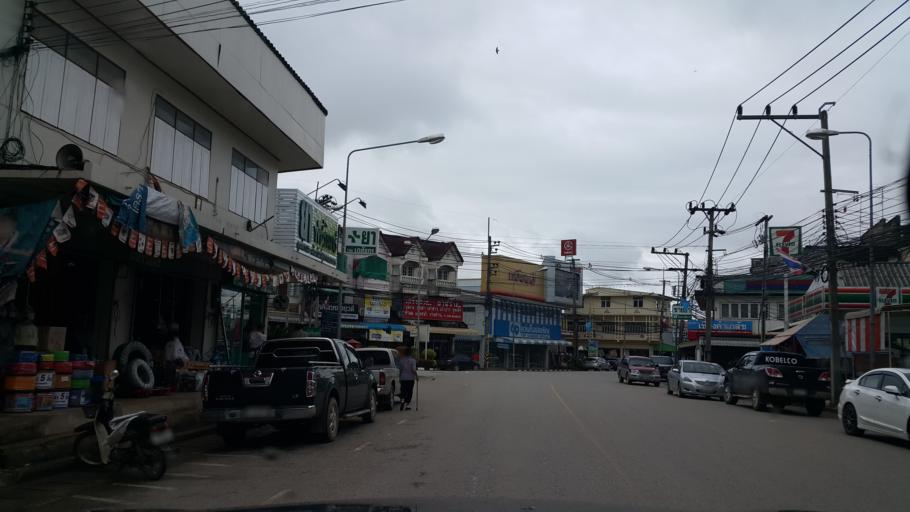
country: TH
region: Phayao
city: Chiang Kham
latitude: 19.5258
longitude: 100.3031
